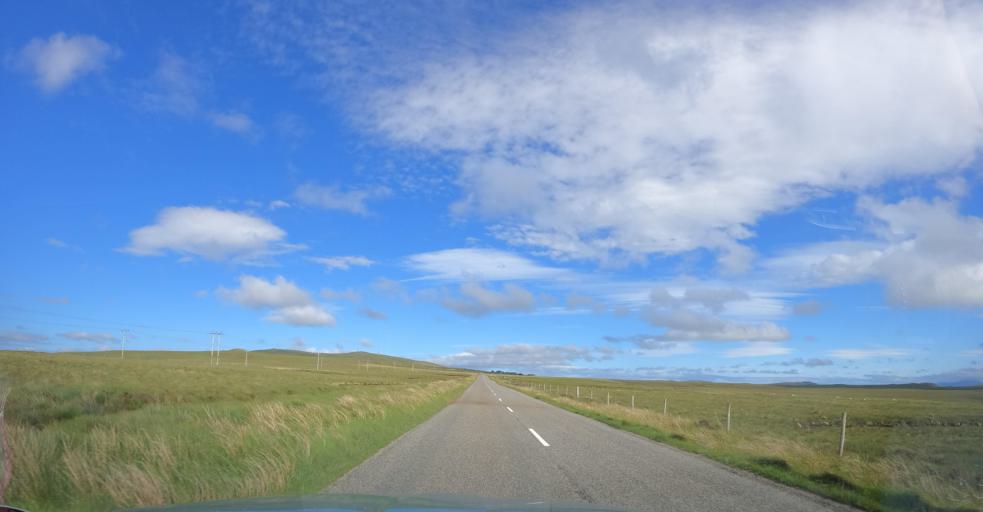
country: GB
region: Scotland
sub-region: Eilean Siar
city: Isle of Lewis
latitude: 58.1781
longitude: -6.6336
